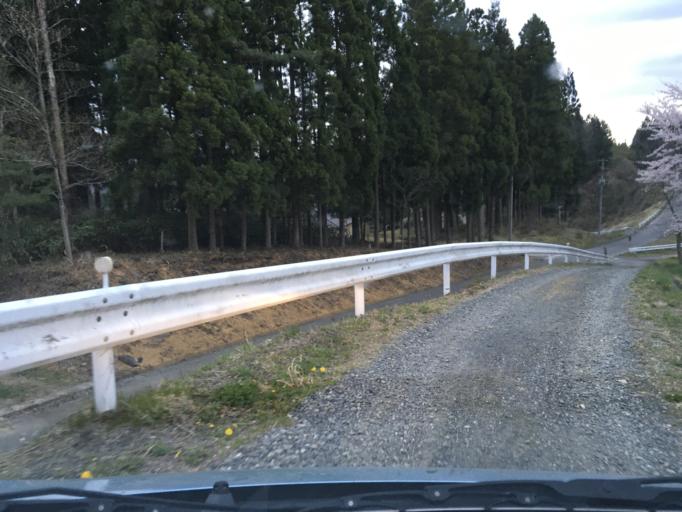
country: JP
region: Iwate
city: Ichinoseki
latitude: 38.9586
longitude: 141.2083
